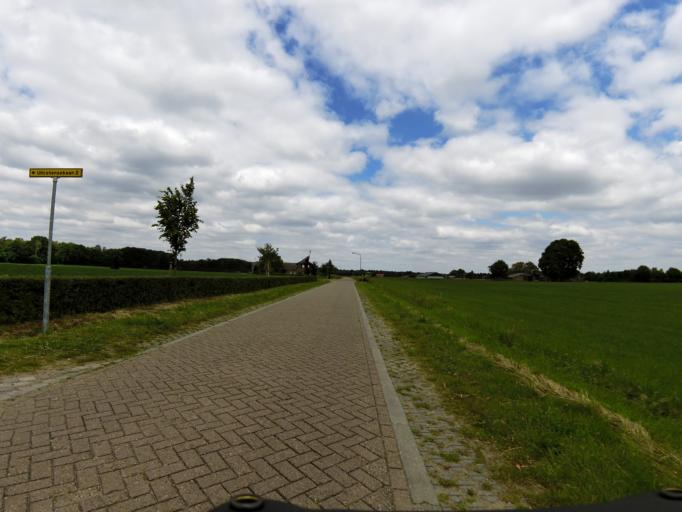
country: NL
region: North Brabant
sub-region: Gemeente Baarle-Nassau
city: Baarle-Nassau
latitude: 51.4793
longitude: 4.9406
